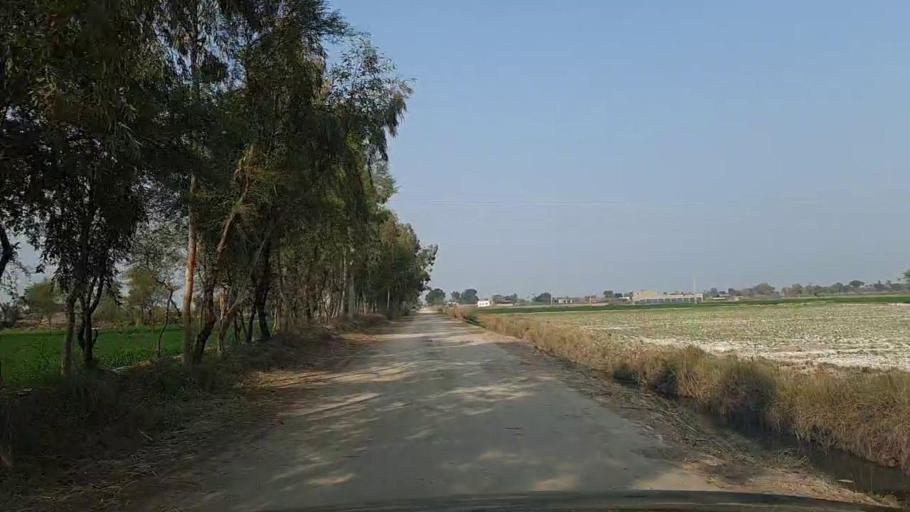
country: PK
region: Sindh
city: Daur
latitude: 26.3937
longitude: 68.4237
